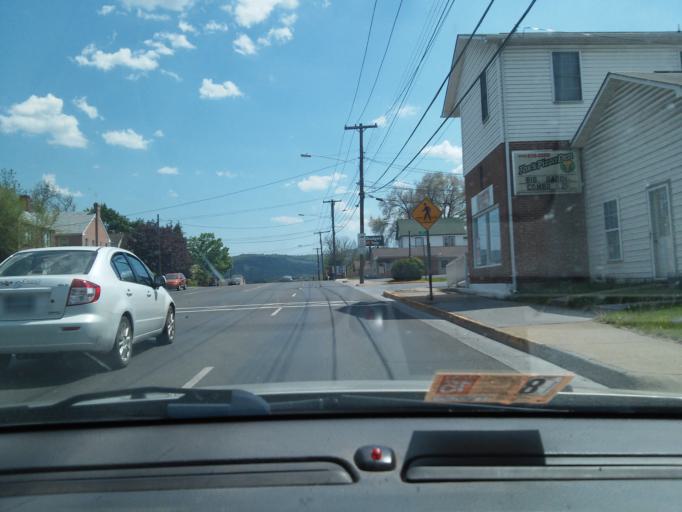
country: US
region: Virginia
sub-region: Warren County
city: Front Royal
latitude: 38.9335
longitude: -78.1945
